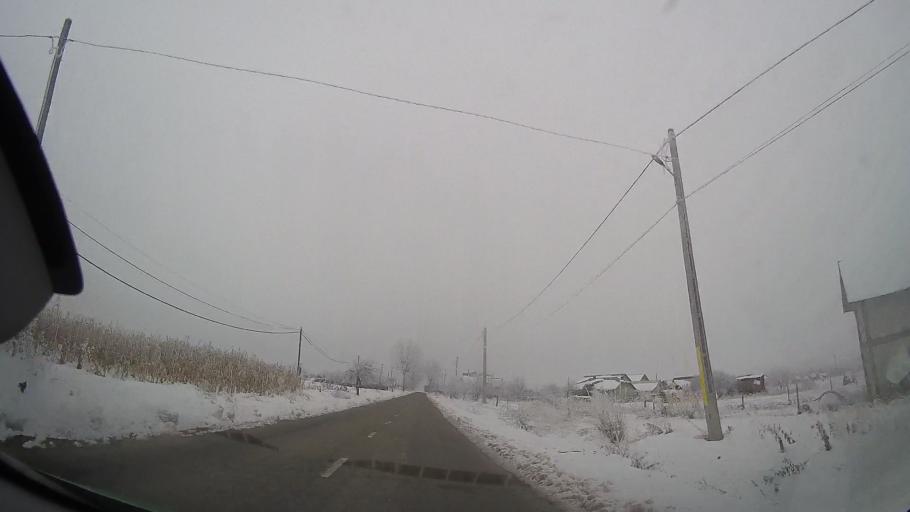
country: RO
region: Neamt
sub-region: Comuna Icusesti
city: Balusesti
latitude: 46.8655
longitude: 27.0004
